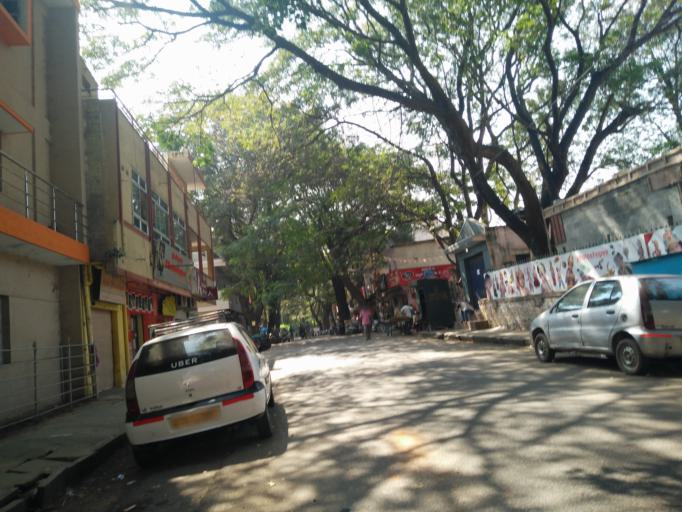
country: IN
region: Karnataka
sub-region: Bangalore Urban
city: Bangalore
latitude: 12.9711
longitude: 77.5437
